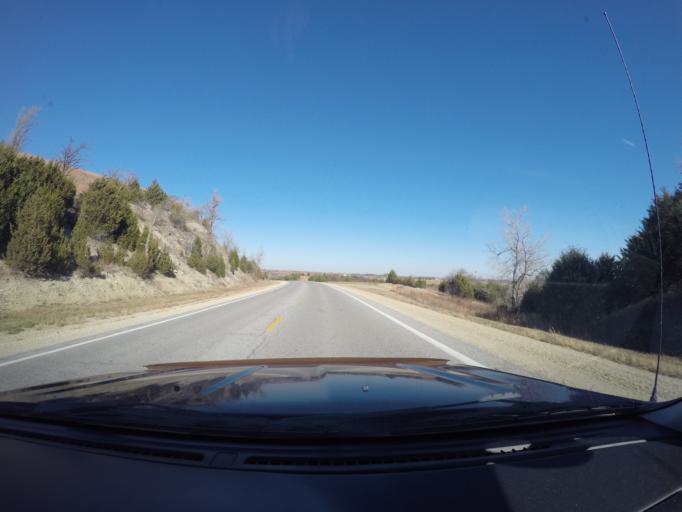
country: US
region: Kansas
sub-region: Riley County
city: Manhattan
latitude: 39.2294
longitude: -96.6188
